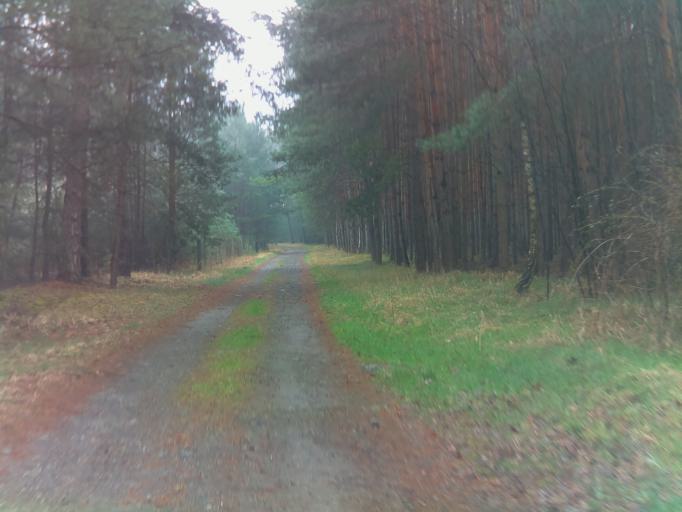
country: DE
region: Brandenburg
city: Lieberose
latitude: 52.0230
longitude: 14.2367
